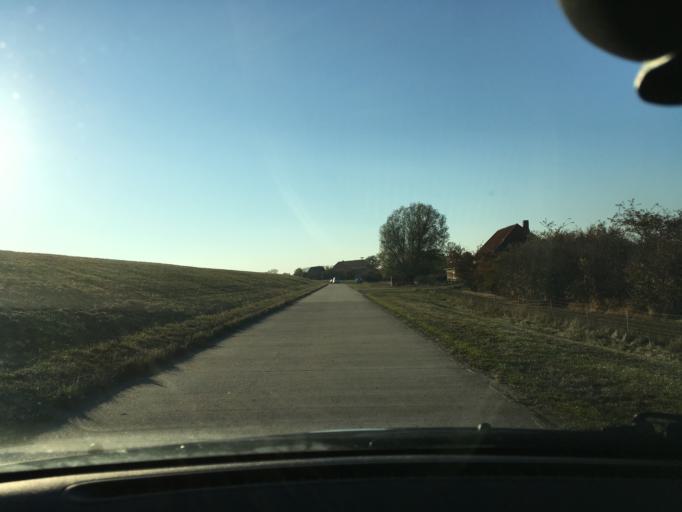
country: DE
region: Lower Saxony
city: Tosterglope
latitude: 53.2855
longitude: 10.8112
